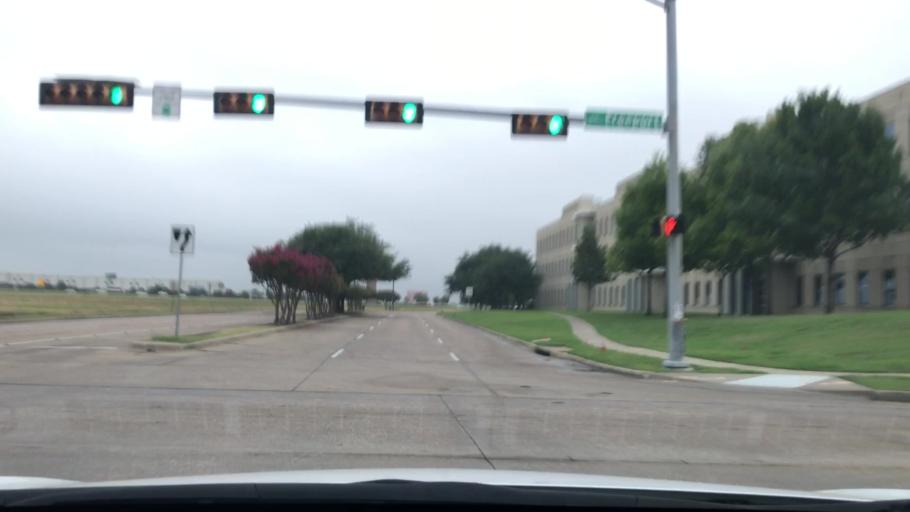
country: US
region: Texas
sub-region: Dallas County
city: Coppell
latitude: 32.9301
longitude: -97.0092
